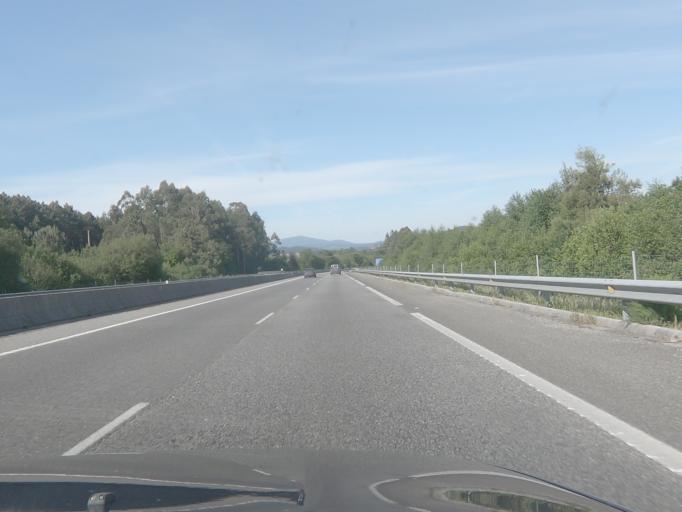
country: ES
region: Galicia
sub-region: Provincia de Pontevedra
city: Meis
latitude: 42.5034
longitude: -8.7192
